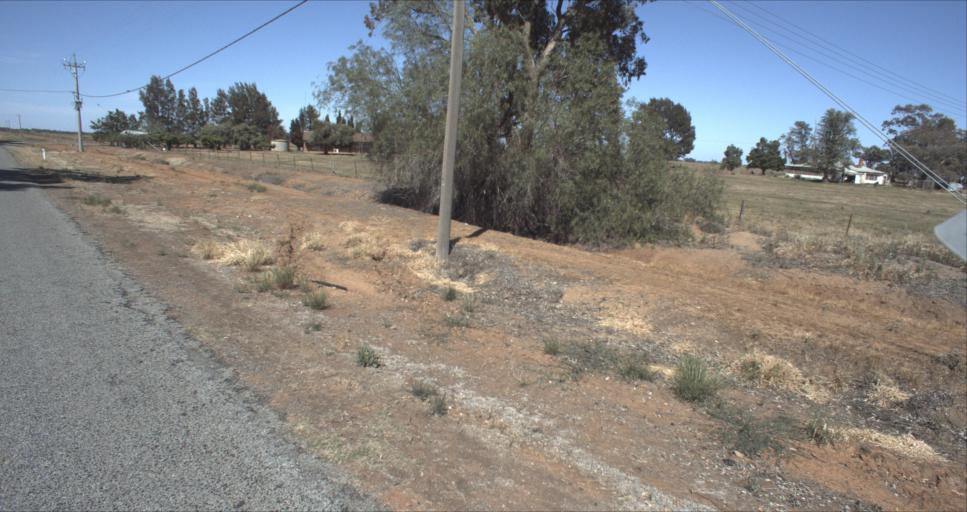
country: AU
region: New South Wales
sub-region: Leeton
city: Leeton
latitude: -34.5436
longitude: 146.3160
